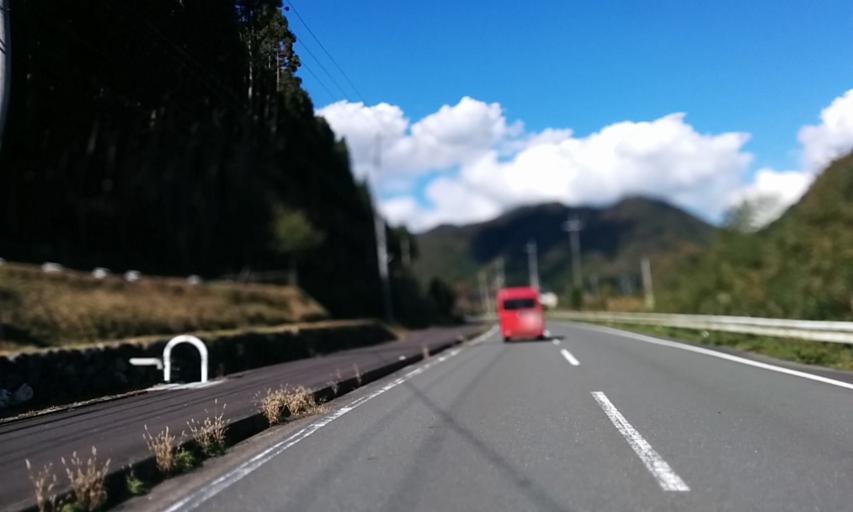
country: JP
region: Kyoto
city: Kameoka
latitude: 35.2624
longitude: 135.5508
